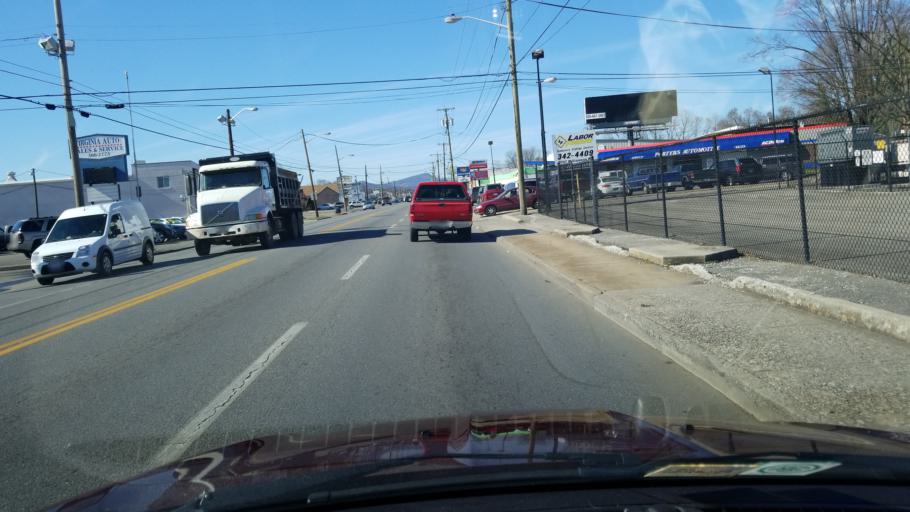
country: US
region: Virginia
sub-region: City of Roanoke
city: Roanoke
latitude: 37.2958
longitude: -79.9368
